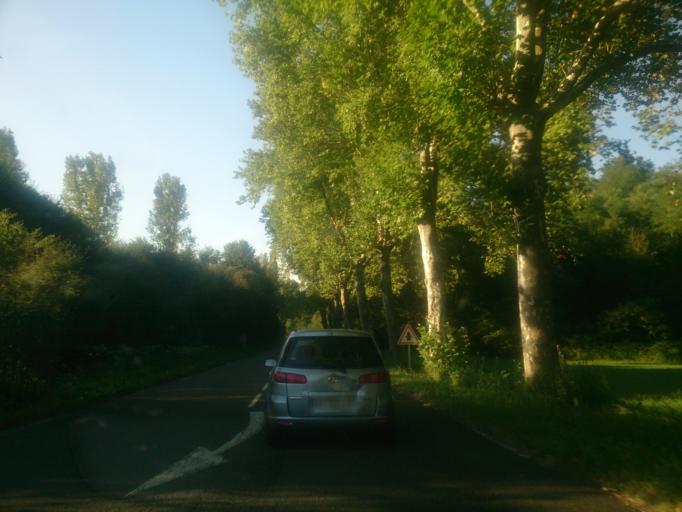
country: FR
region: Limousin
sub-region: Departement de la Correze
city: Brive-la-Gaillarde
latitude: 45.1176
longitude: 1.5187
